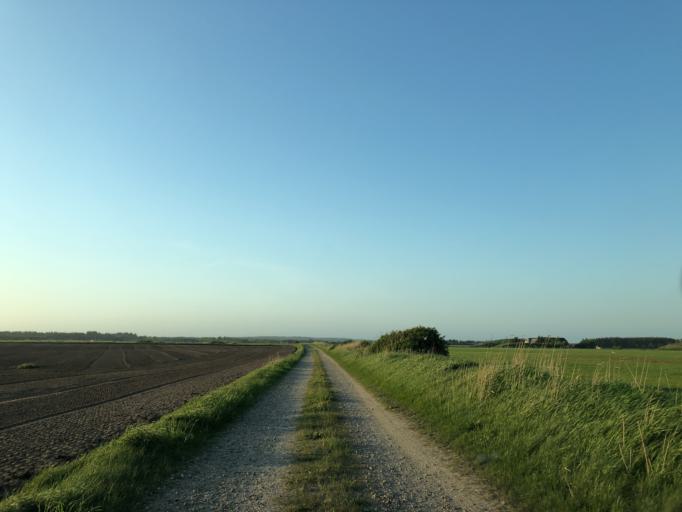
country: DK
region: Central Jutland
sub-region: Holstebro Kommune
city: Ulfborg
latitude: 56.2493
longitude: 8.1527
